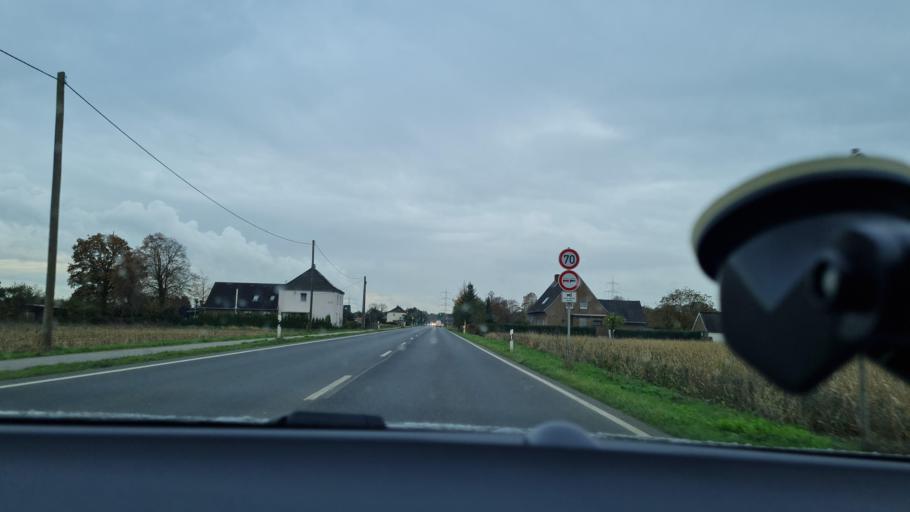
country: DE
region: North Rhine-Westphalia
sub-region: Regierungsbezirk Dusseldorf
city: Voerde
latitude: 51.6127
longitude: 6.6505
